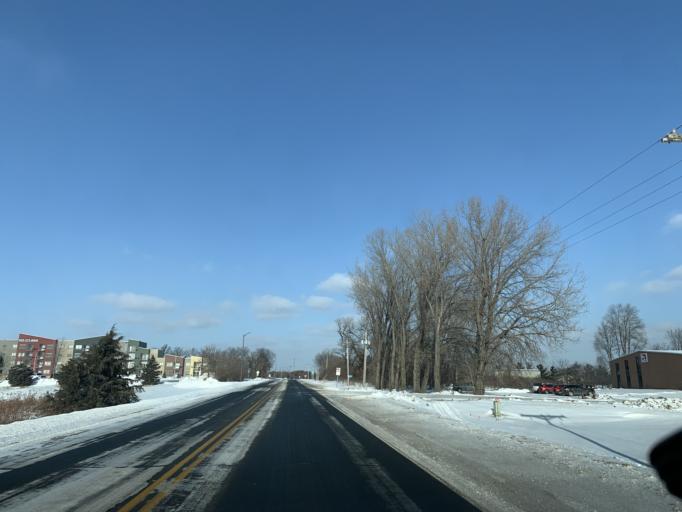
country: US
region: Minnesota
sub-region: Scott County
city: Prior Lake
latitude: 44.7785
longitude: -93.4062
